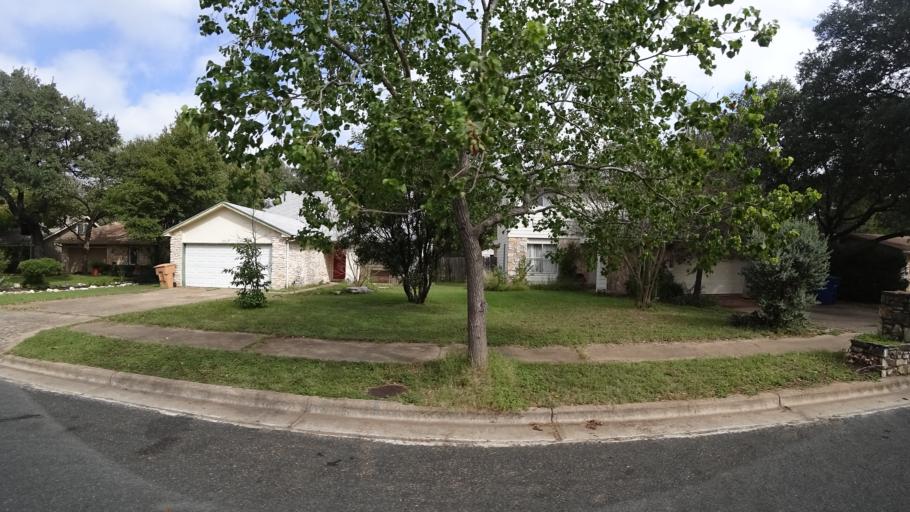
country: US
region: Texas
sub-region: Travis County
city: Shady Hollow
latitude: 30.2073
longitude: -97.8337
